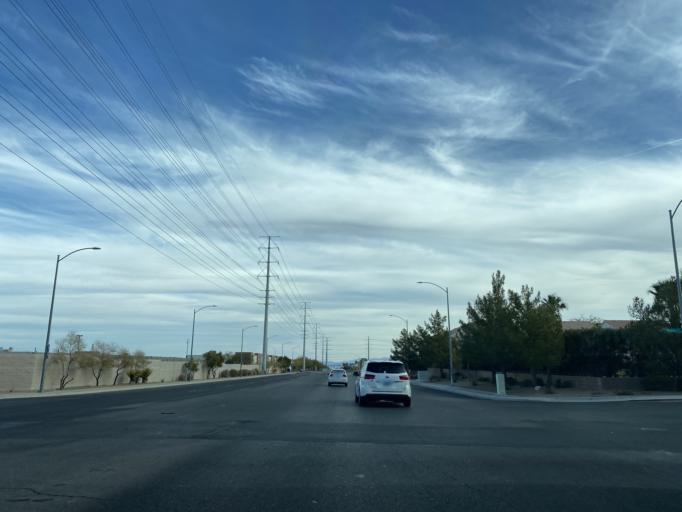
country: US
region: Nevada
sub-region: Clark County
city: Enterprise
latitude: 36.0556
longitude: -115.2500
